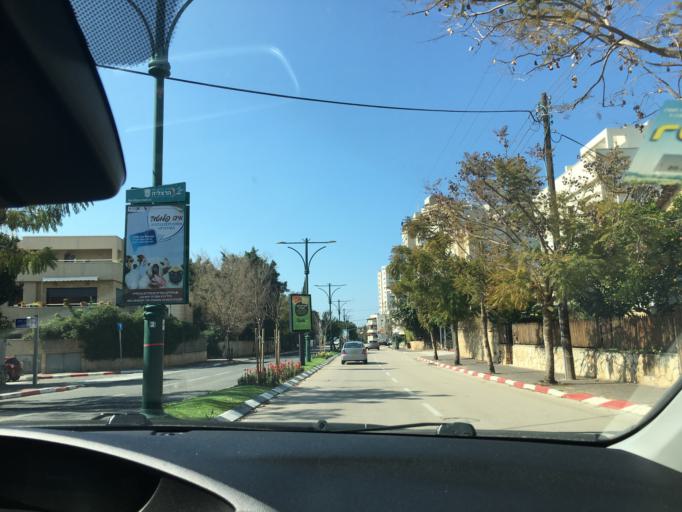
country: IL
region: Tel Aviv
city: Ramat HaSharon
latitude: 32.1603
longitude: 34.8446
